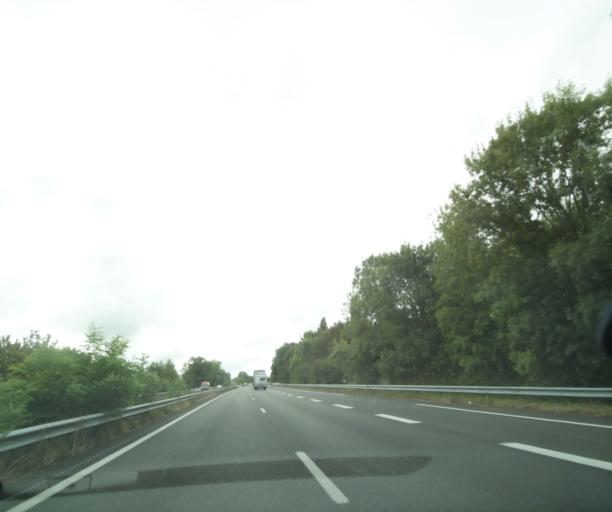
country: FR
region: Poitou-Charentes
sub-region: Departement de la Charente-Maritime
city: Saint-Genis-de-Saintonge
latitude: 45.4383
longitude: -0.6064
